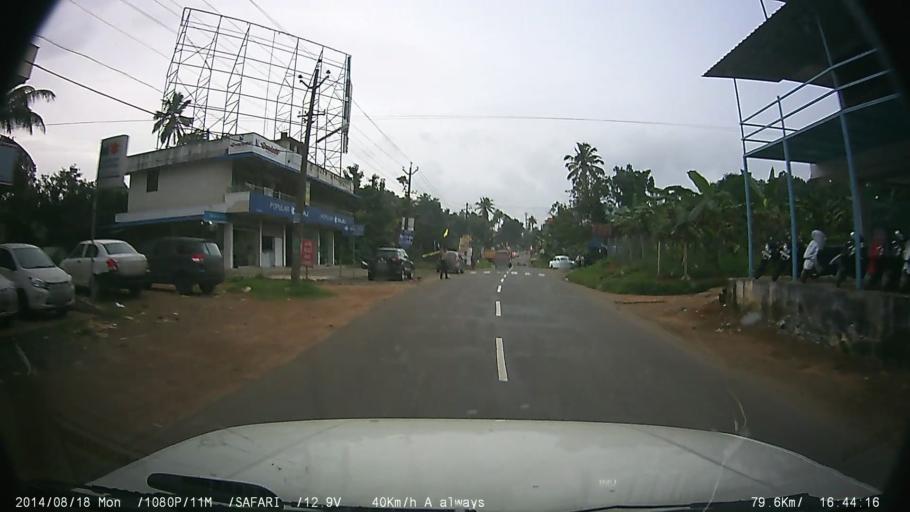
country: IN
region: Kerala
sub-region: Ernakulam
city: Piravam
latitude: 9.8518
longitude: 76.5924
